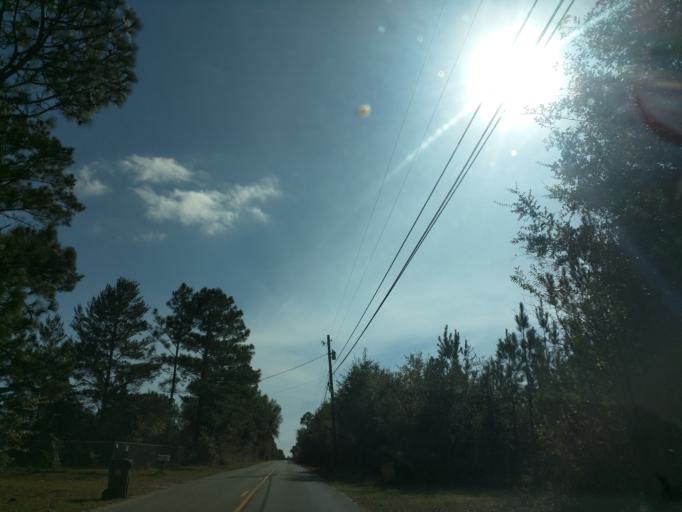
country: US
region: Florida
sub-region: Escambia County
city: Cantonment
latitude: 30.5466
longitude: -87.4058
